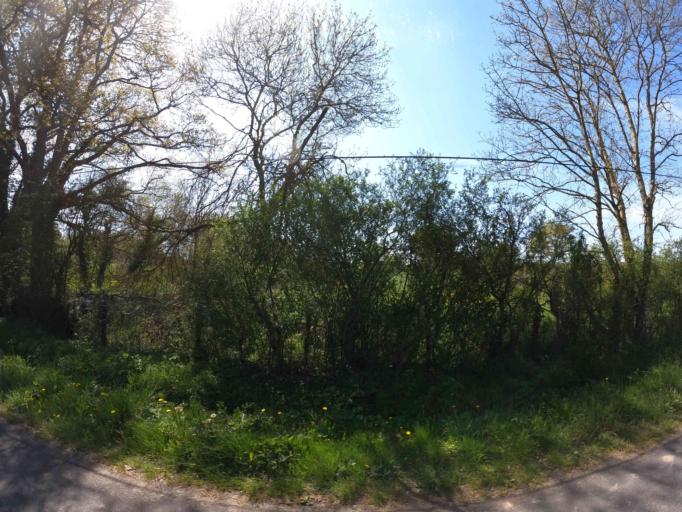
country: FR
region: Pays de la Loire
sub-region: Departement de la Loire-Atlantique
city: Remouille
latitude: 47.0268
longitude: -1.3827
